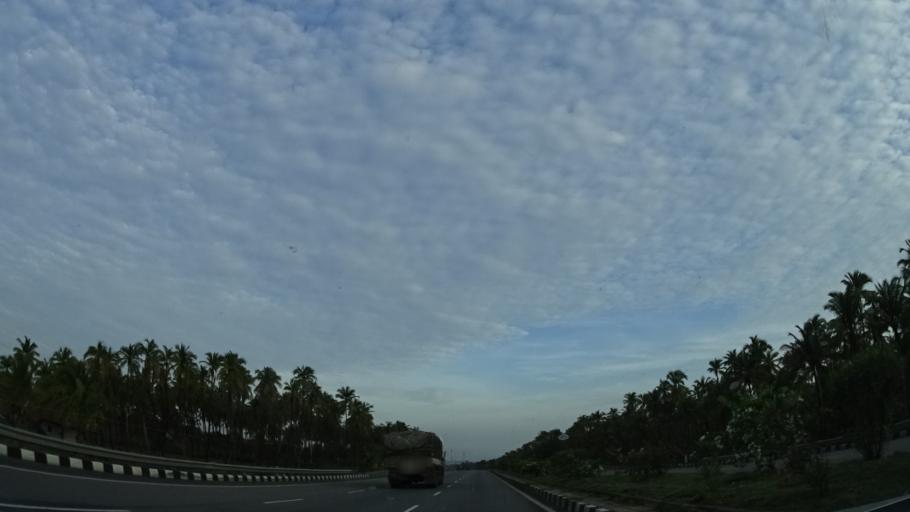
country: IN
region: Karnataka
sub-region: Chitradurga
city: Hiriyur
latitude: 13.9019
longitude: 76.6706
